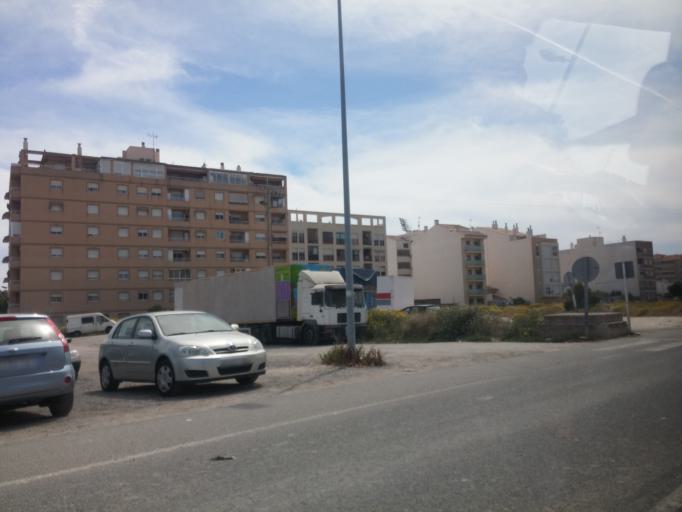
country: ES
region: Valencia
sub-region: Provincia de Alicante
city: Villajoyosa
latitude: 38.5037
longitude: -0.2392
